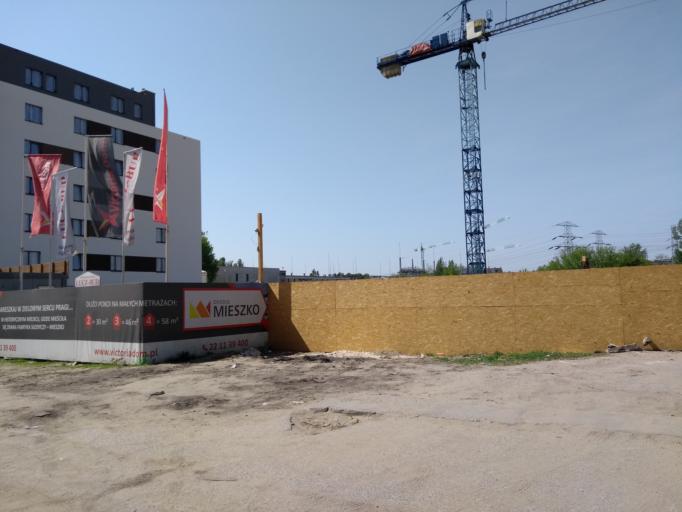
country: PL
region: Masovian Voivodeship
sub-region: Warszawa
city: Praga Poludnie
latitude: 52.2544
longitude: 21.0816
